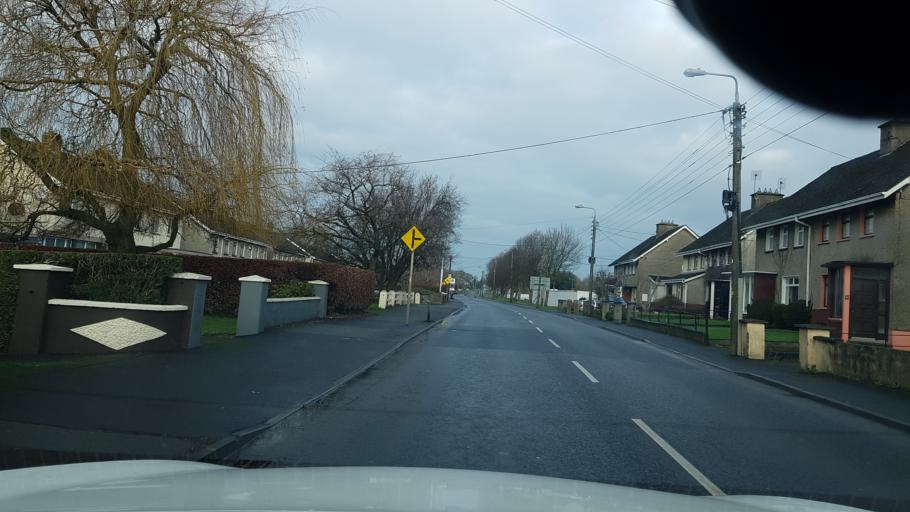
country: IE
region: Leinster
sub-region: An Mhi
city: Navan
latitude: 53.6601
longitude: -6.6797
